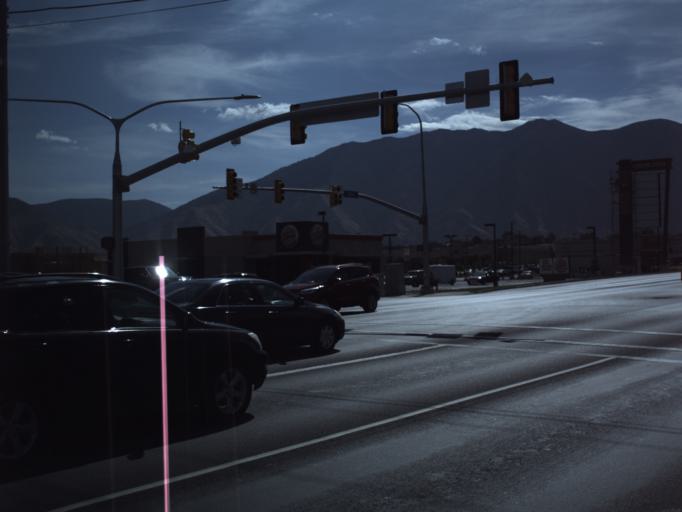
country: US
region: Utah
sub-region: Utah County
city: Spanish Fork
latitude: 40.1234
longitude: -111.6440
